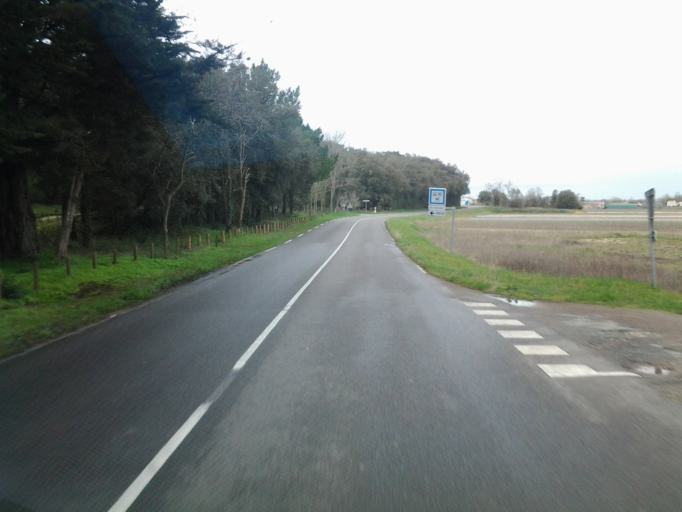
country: FR
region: Pays de la Loire
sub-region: Departement de la Vendee
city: La Tranche-sur-Mer
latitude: 46.3817
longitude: -1.4658
